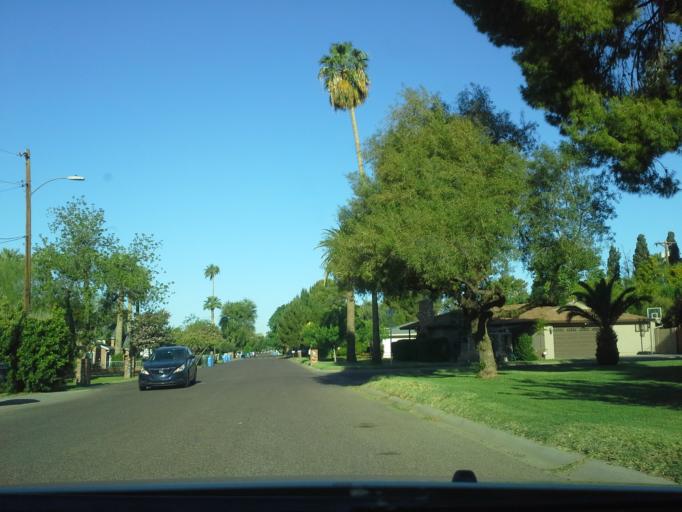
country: US
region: Arizona
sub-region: Maricopa County
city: Phoenix
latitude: 33.5420
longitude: -112.0843
